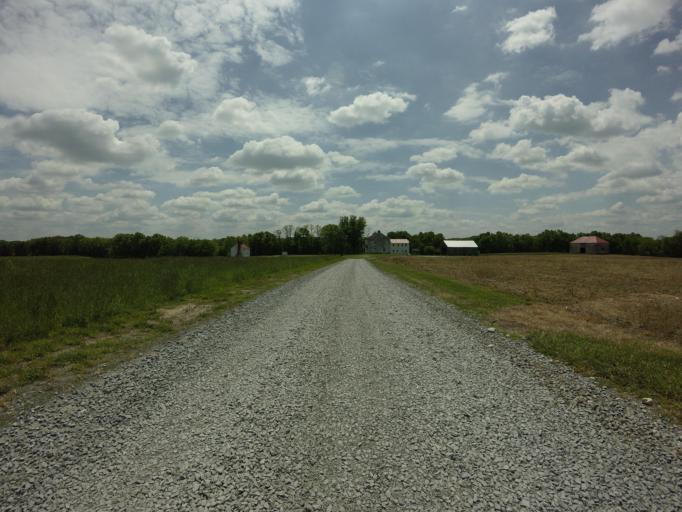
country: US
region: Maryland
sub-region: Frederick County
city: Ballenger Creek
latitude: 39.3721
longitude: -77.3990
